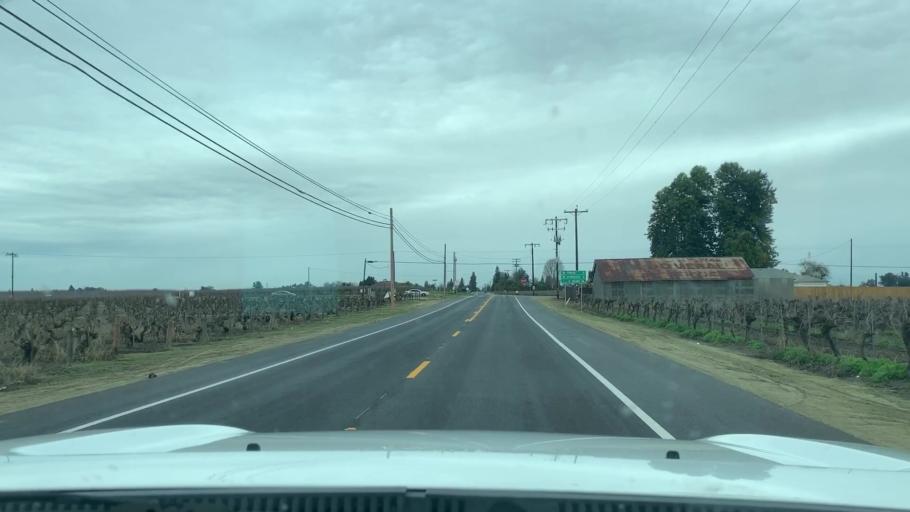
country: US
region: California
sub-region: Fresno County
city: Fowler
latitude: 36.5604
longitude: -119.6824
